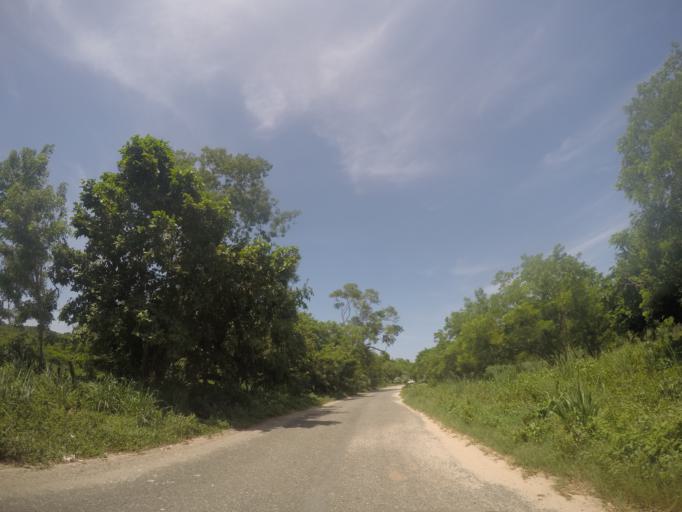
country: MX
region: Oaxaca
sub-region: Villa de Tututepec de Melchor Ocampo
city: Santa Rosa de Lima
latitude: 15.9922
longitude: -97.5389
